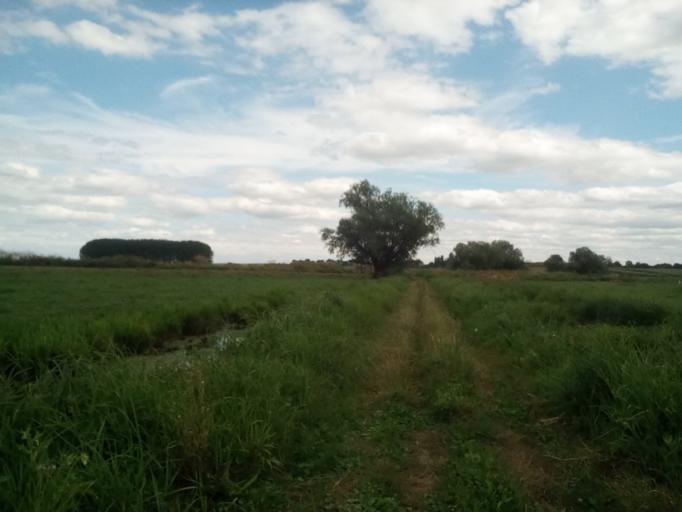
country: FR
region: Lower Normandy
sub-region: Departement du Calvados
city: Troarn
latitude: 49.1733
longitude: -0.1547
